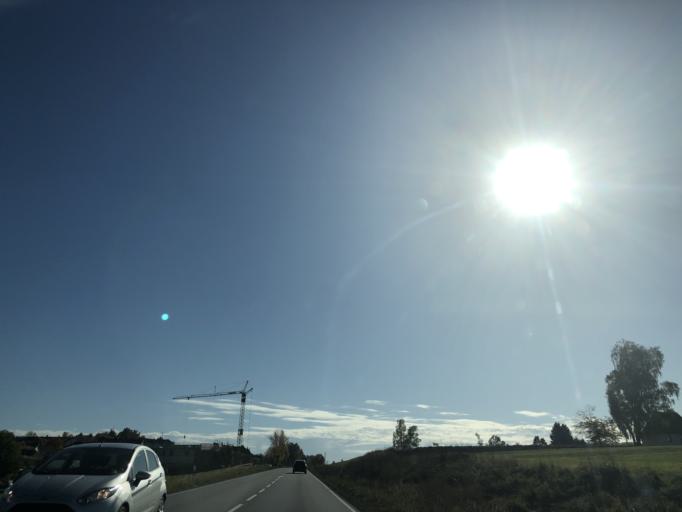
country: DE
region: Bavaria
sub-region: Lower Bavaria
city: Ruhmannsfelden
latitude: 48.9813
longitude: 12.9806
